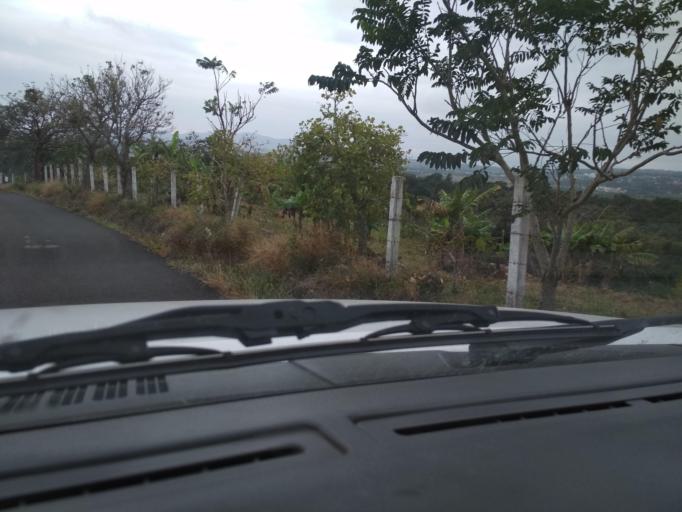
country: MX
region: Veracruz
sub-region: Emiliano Zapata
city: Dos Rios
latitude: 19.5154
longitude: -96.7925
